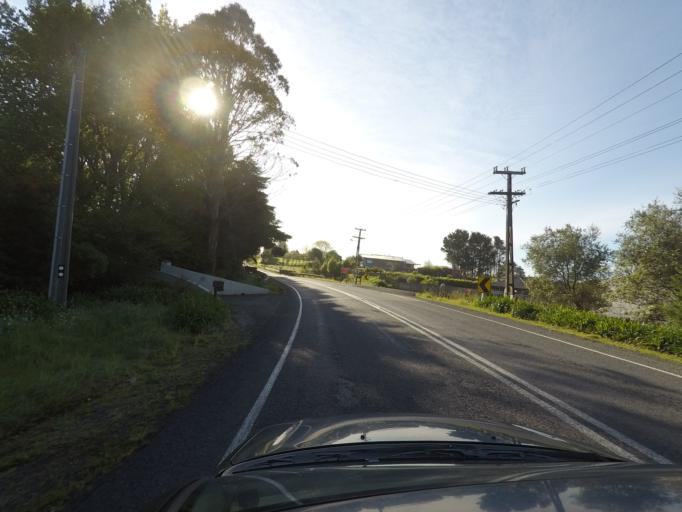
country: NZ
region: Auckland
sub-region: Auckland
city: Takanini
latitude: -37.0180
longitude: 174.9267
